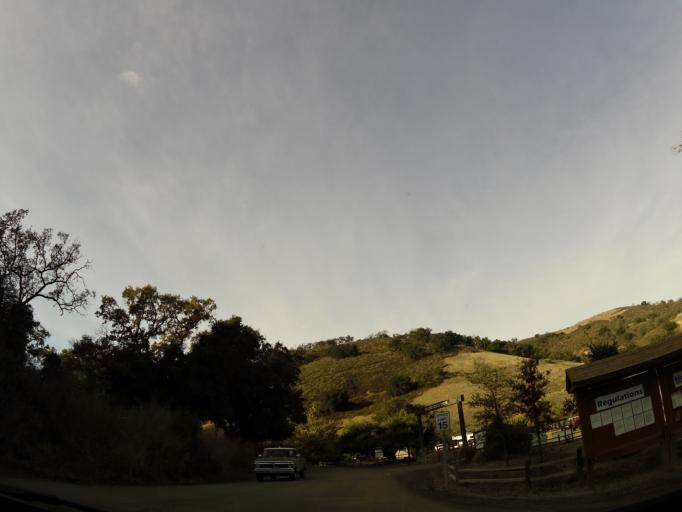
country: US
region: California
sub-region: San Benito County
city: Ridgemark
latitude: 36.7708
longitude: -121.4146
